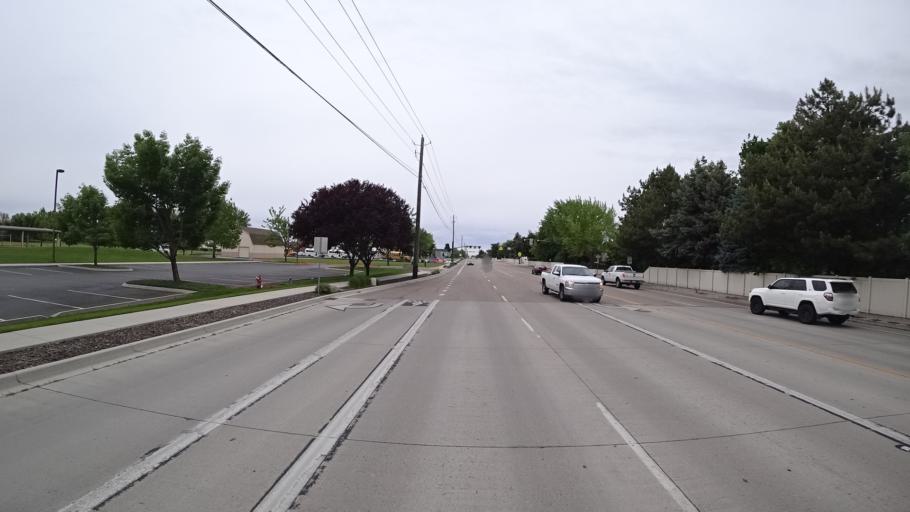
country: US
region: Idaho
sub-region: Ada County
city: Meridian
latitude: 43.6338
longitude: -116.3357
